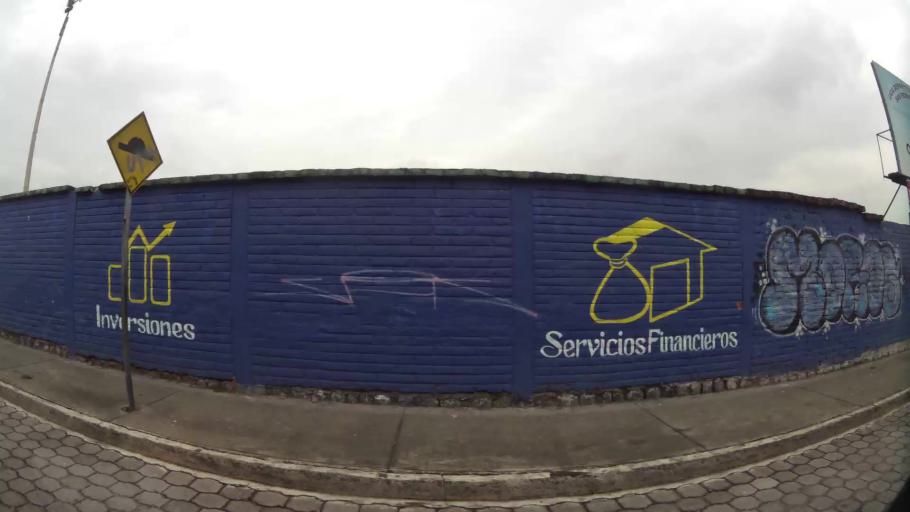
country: EC
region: Pichincha
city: Sangolqui
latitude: -0.3242
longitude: -78.4614
